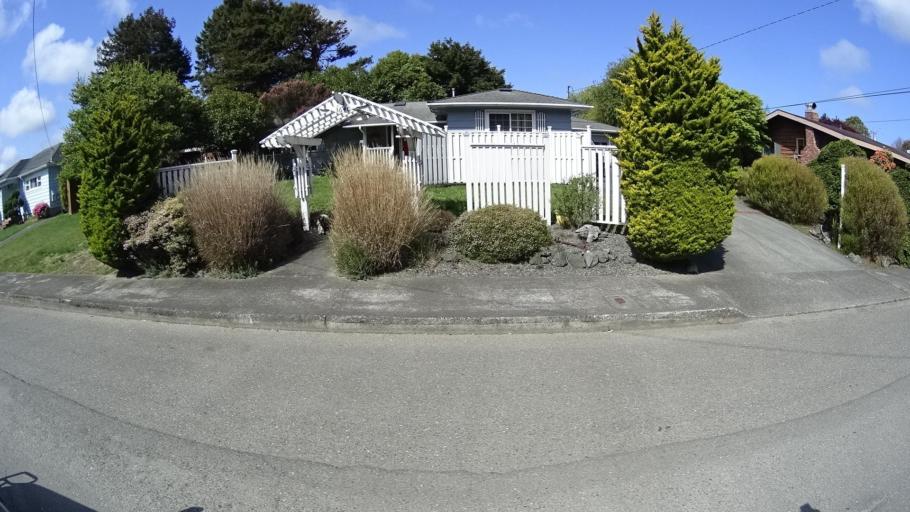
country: US
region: California
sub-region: Humboldt County
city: Cutten
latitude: 40.7738
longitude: -124.1614
